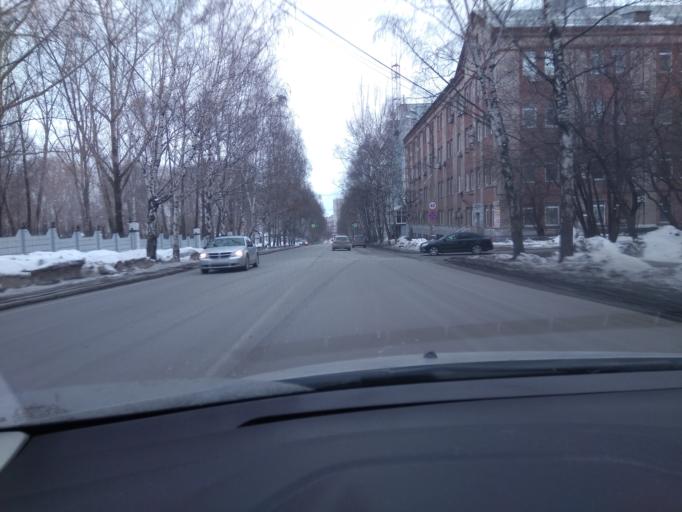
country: RU
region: Sverdlovsk
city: Yekaterinburg
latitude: 56.8484
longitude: 60.6354
